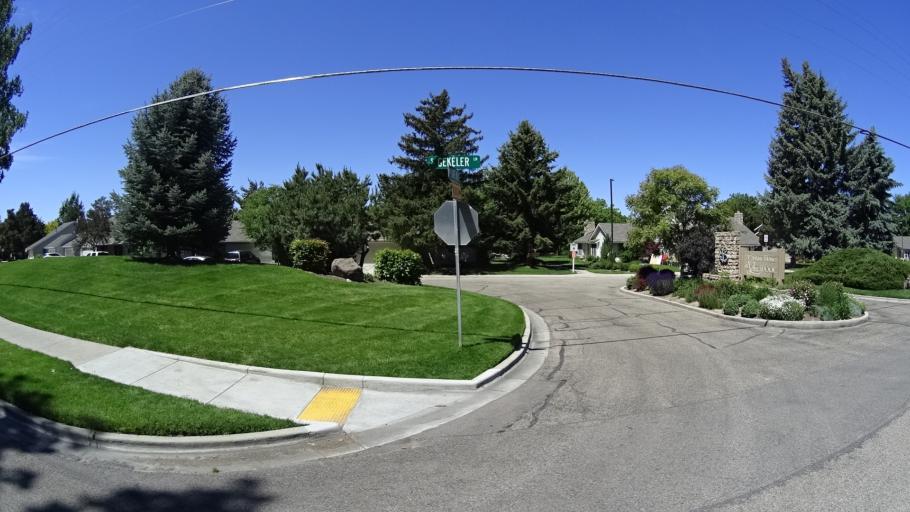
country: US
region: Idaho
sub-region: Ada County
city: Boise
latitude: 43.5744
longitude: -116.1836
